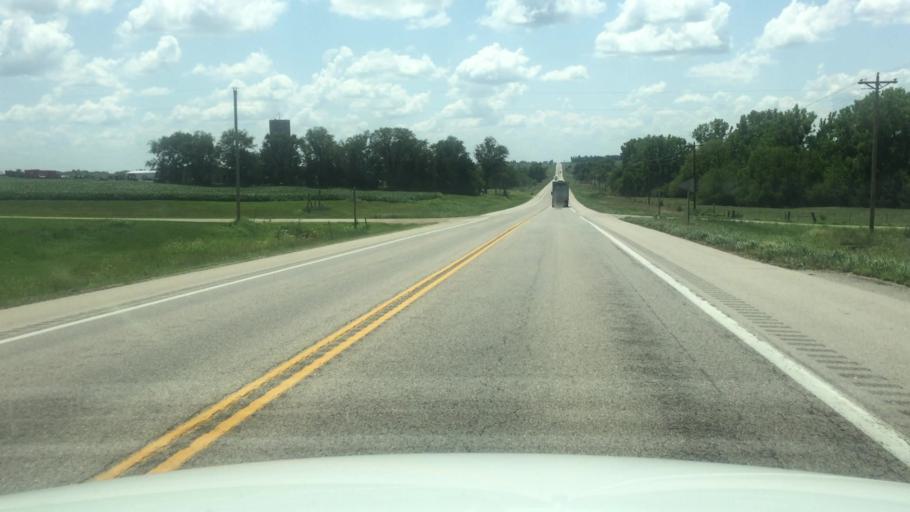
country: US
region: Kansas
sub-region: Brown County
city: Horton
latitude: 39.6972
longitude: -95.7303
